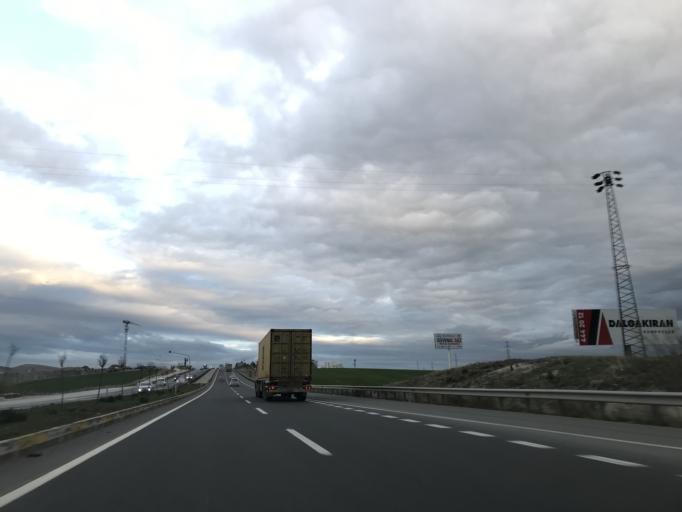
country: TR
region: Ankara
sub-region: Goelbasi
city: Golbasi
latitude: 39.6414
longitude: 32.8248
